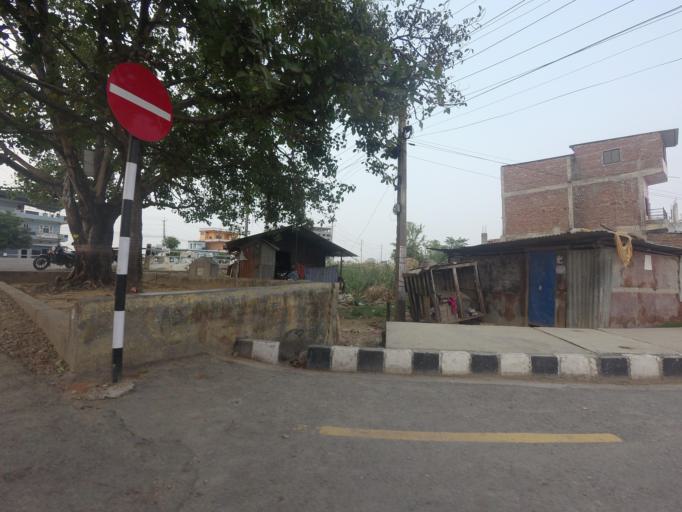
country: NP
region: Western Region
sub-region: Lumbini Zone
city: Bhairahawa
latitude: 27.5094
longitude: 83.4187
